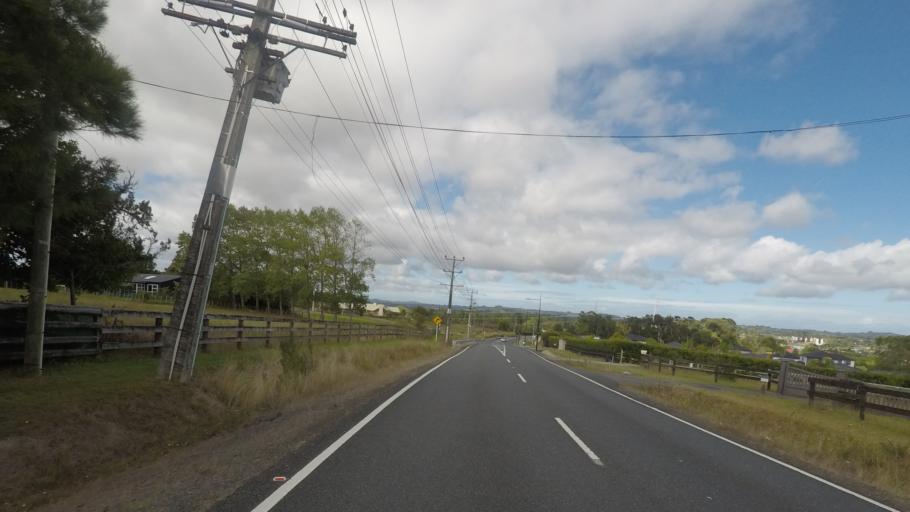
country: NZ
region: Auckland
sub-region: Auckland
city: Muriwai Beach
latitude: -36.7664
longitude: 174.5563
